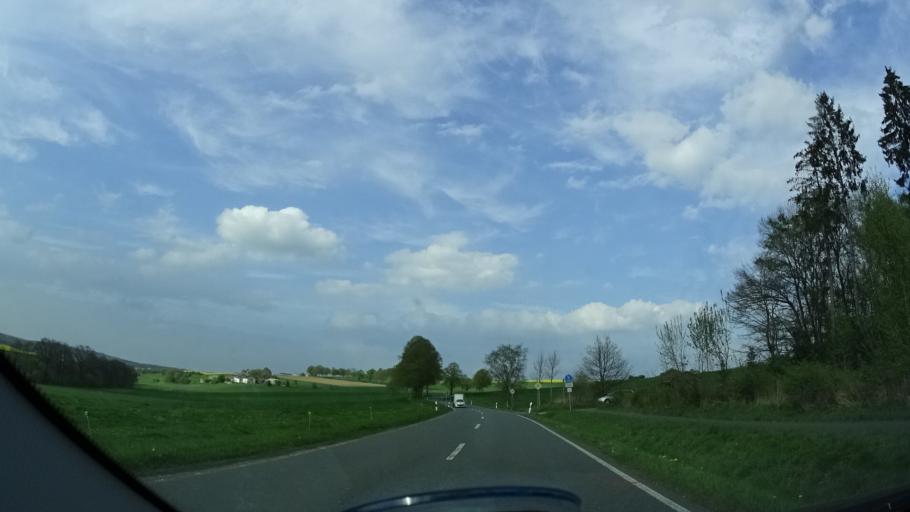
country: DE
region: North Rhine-Westphalia
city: Warstein
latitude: 51.4304
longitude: 8.3258
